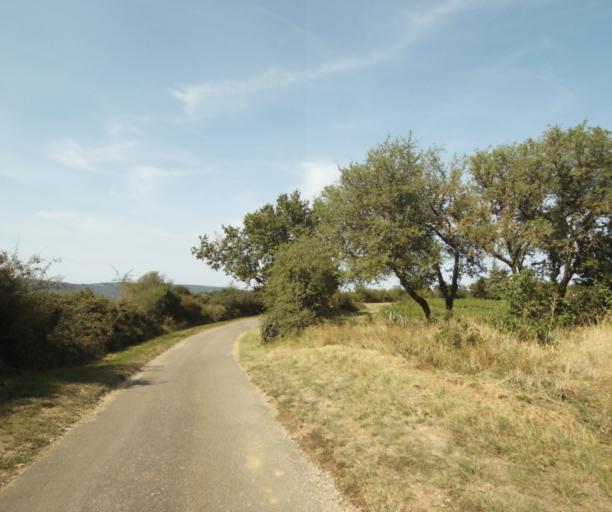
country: FR
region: Bourgogne
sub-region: Departement de Saone-et-Loire
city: Tournus
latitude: 46.5570
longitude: 4.8727
